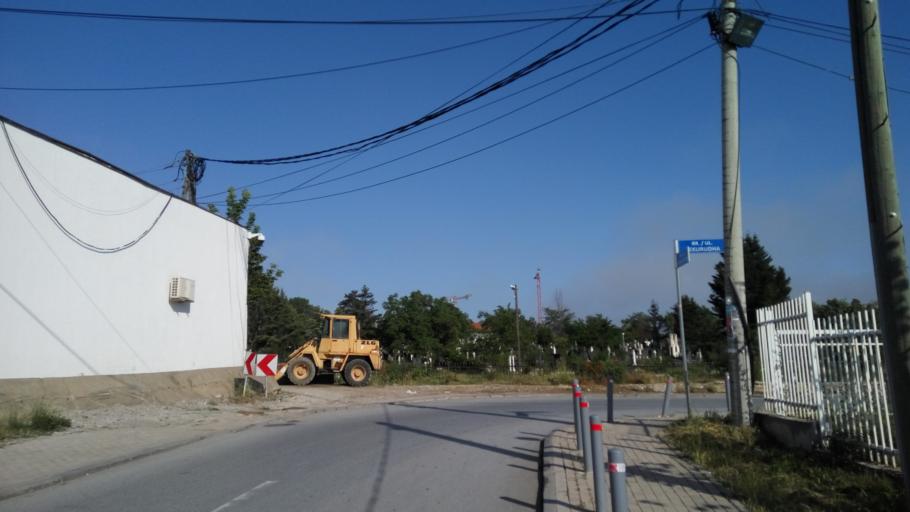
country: XK
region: Pristina
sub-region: Komuna e Prishtines
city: Pristina
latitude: 42.6542
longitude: 21.1466
